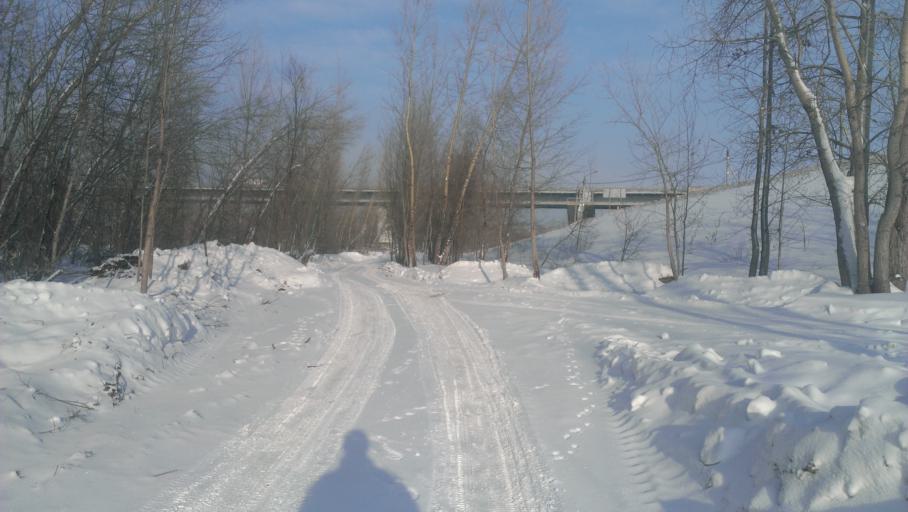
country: RU
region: Altai Krai
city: Zaton
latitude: 53.3193
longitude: 83.8093
